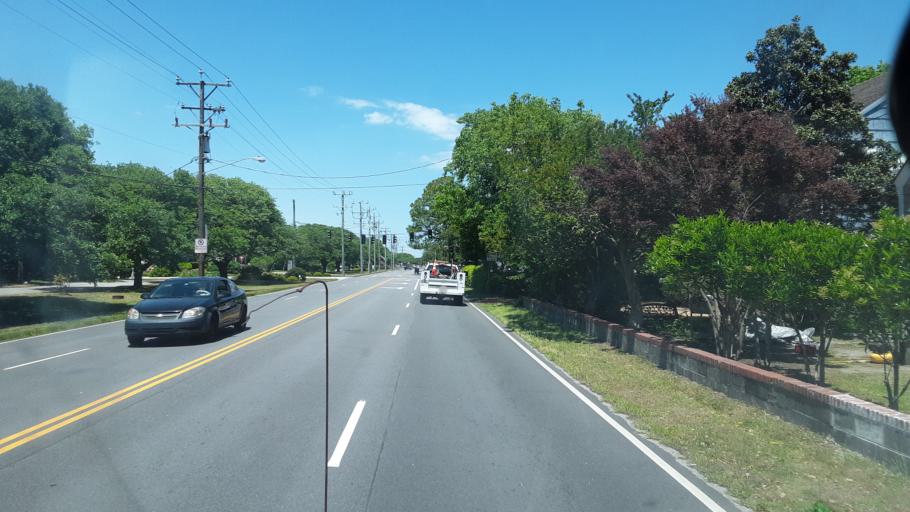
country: US
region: Virginia
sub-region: City of Virginia Beach
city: Virginia Beach
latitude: 36.9010
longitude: -75.9914
